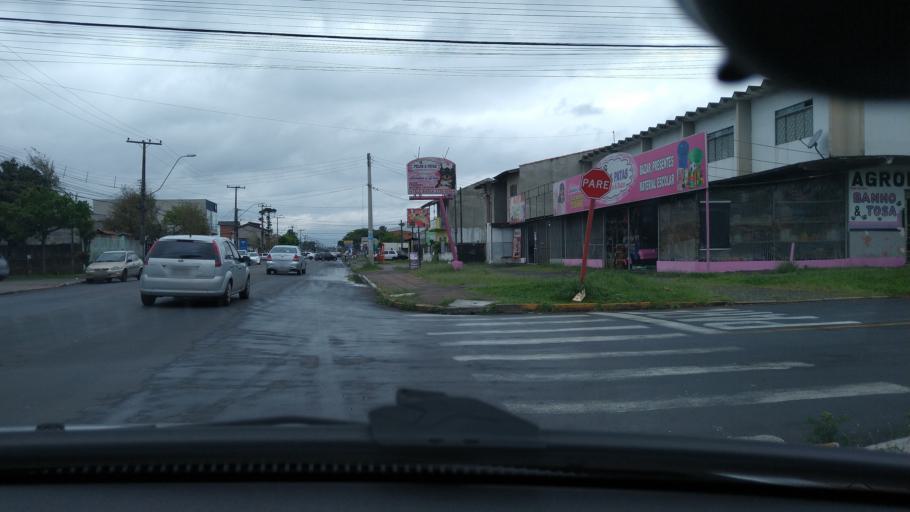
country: BR
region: Rio Grande do Sul
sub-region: Canoas
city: Canoas
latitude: -29.9016
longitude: -51.2131
